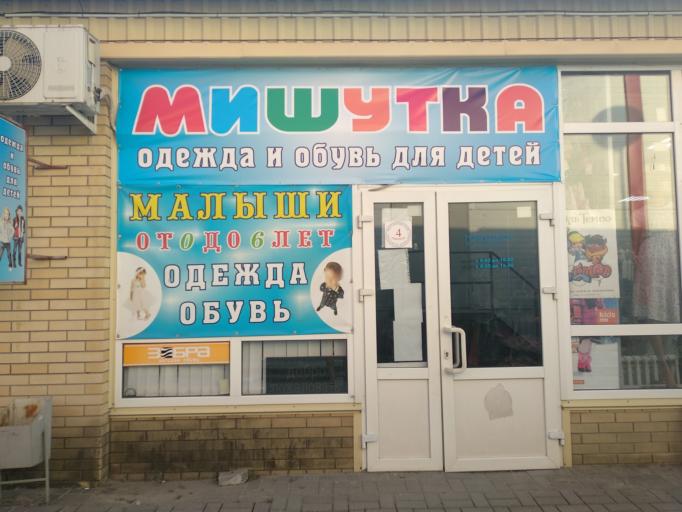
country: RU
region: Rostov
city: Millerovo
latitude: 48.9251
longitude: 40.4008
